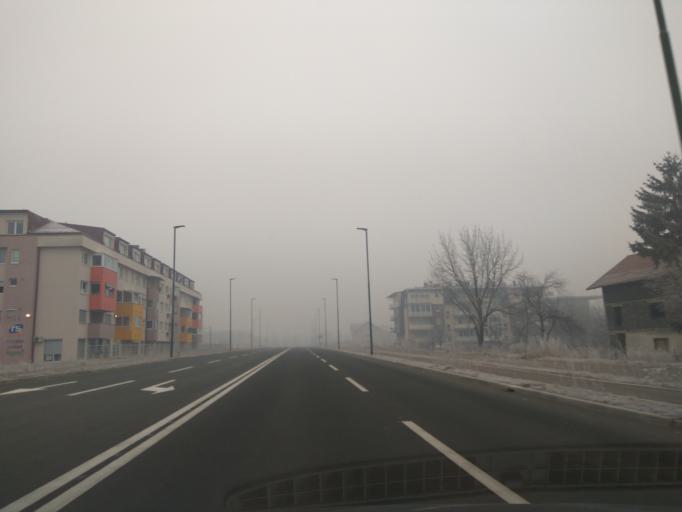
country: BA
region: Federation of Bosnia and Herzegovina
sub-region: Kanton Sarajevo
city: Sarajevo
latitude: 43.8321
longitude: 18.3366
